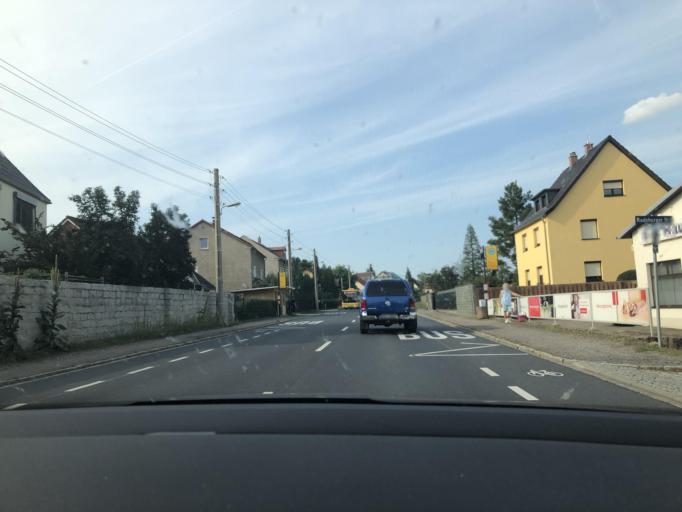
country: DE
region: Saxony
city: Albertstadt
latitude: 51.1135
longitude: 13.7280
